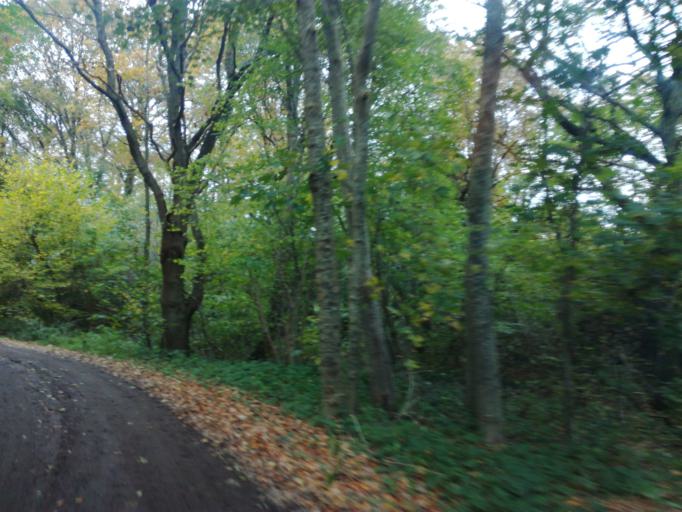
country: DK
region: South Denmark
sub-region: Fredericia Kommune
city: Fredericia
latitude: 55.6000
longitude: 9.7096
